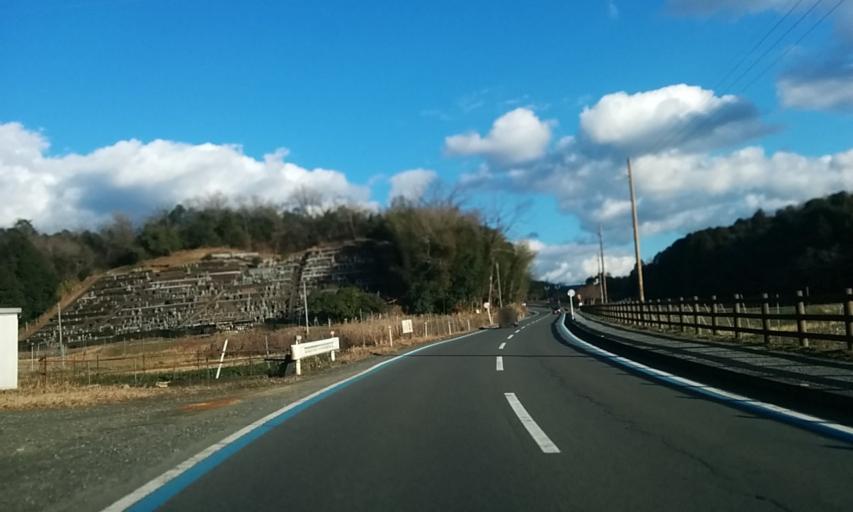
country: JP
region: Kyoto
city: Fukuchiyama
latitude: 35.3173
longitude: 135.1270
